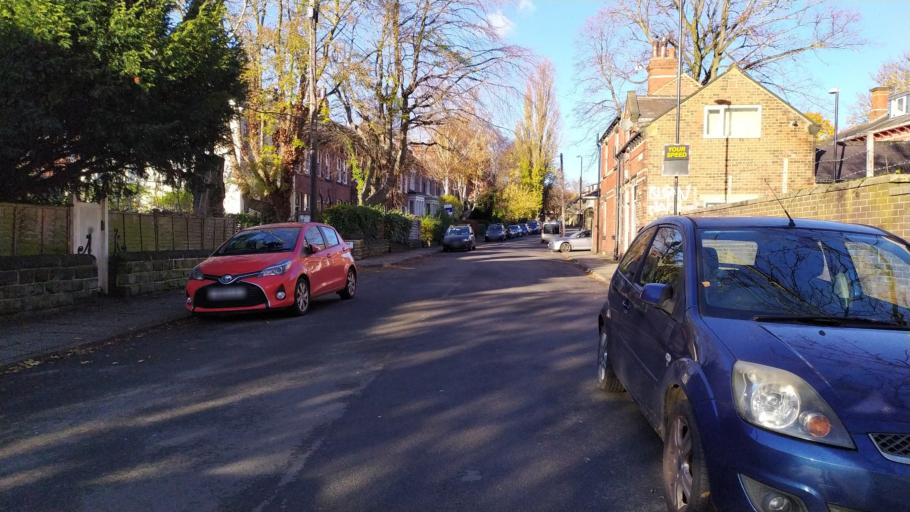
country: GB
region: England
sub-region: City and Borough of Leeds
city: Leeds
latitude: 53.8149
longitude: -1.5776
